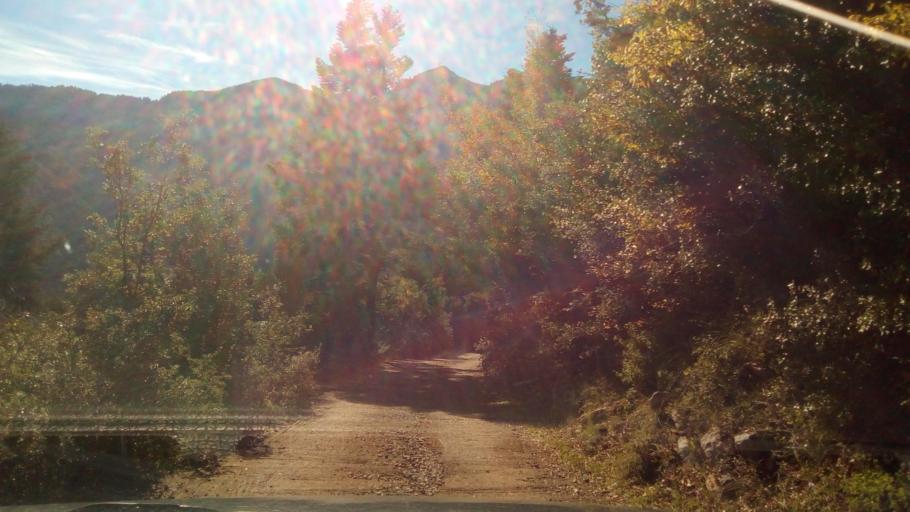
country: GR
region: West Greece
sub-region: Nomos Aitolias kai Akarnanias
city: Nafpaktos
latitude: 38.5931
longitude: 21.8796
